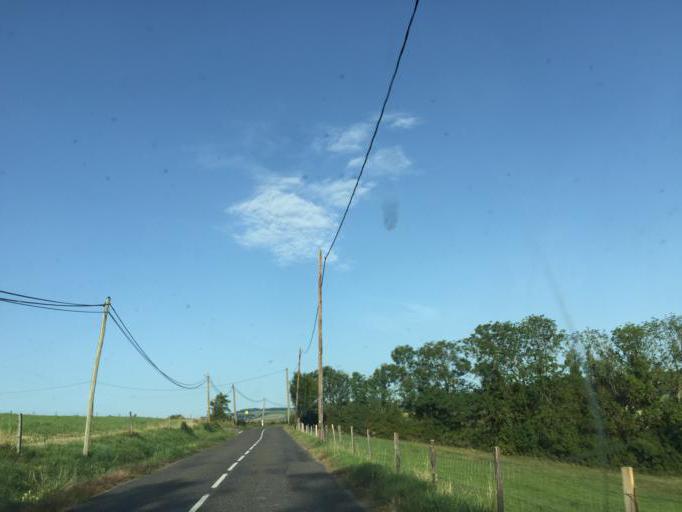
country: FR
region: Rhone-Alpes
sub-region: Departement de la Loire
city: Saint-Christo-en-Jarez
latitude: 45.5219
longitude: 4.4864
